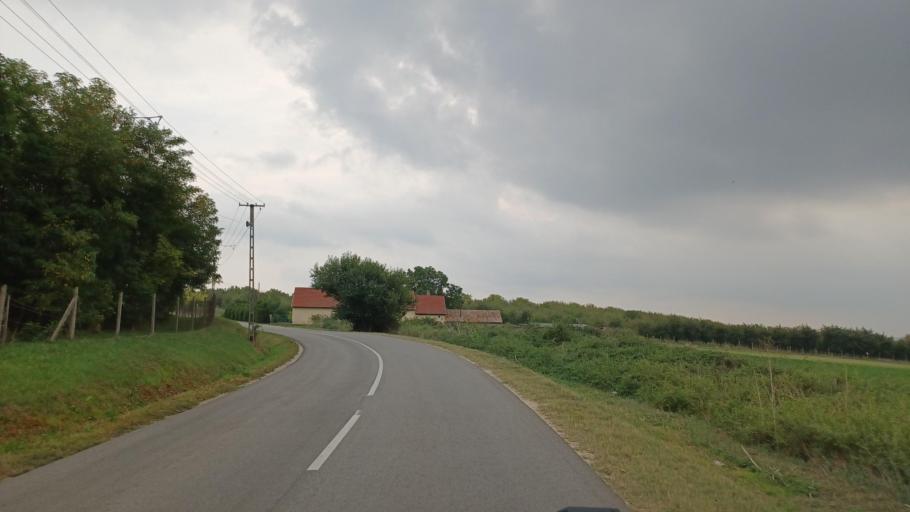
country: HU
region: Tolna
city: Pincehely
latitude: 46.6534
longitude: 18.4123
